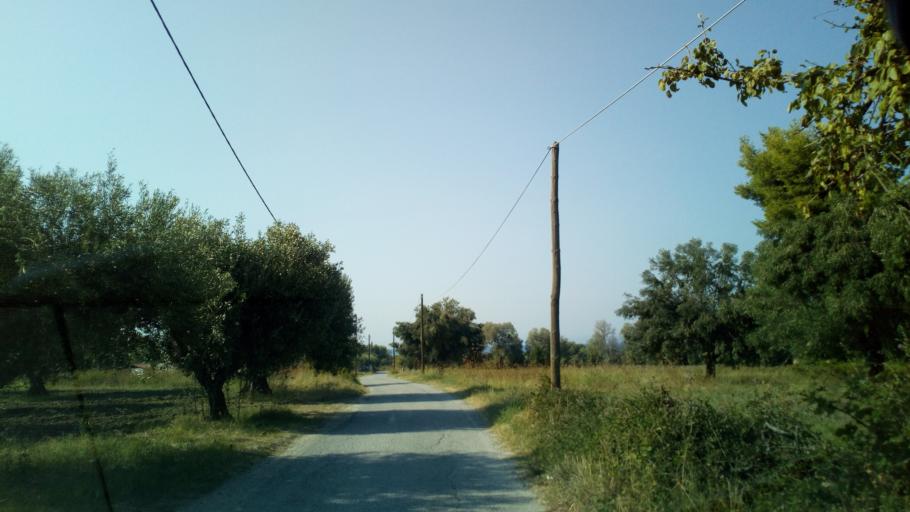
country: GR
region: Central Macedonia
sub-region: Nomos Chalkidikis
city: Pefkochori
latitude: 39.9755
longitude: 23.6521
